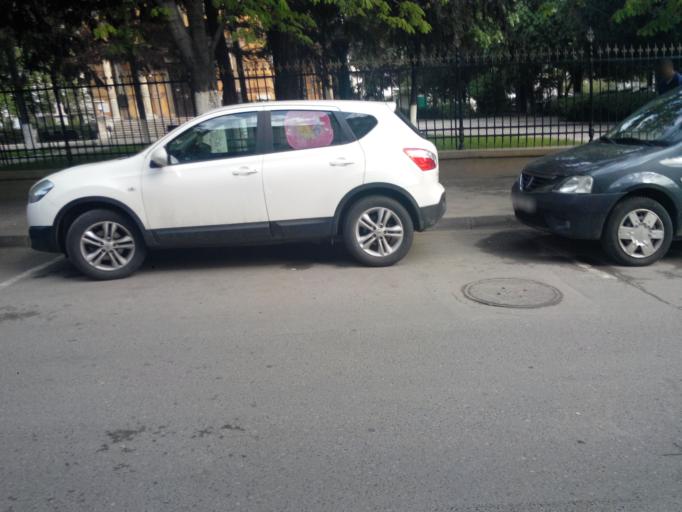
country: RO
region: Bucuresti
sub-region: Municipiul Bucuresti
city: Bucuresti
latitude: 44.4284
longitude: 26.0996
